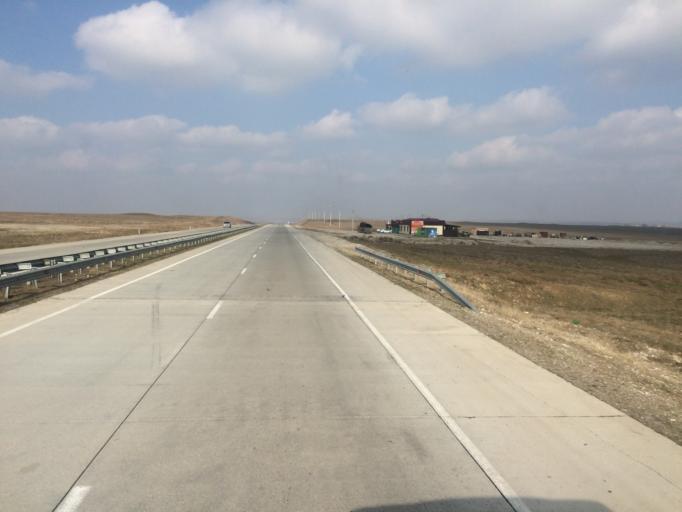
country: KZ
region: Ongtustik Qazaqstan
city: Temirlanovka
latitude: 42.5676
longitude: 69.3108
